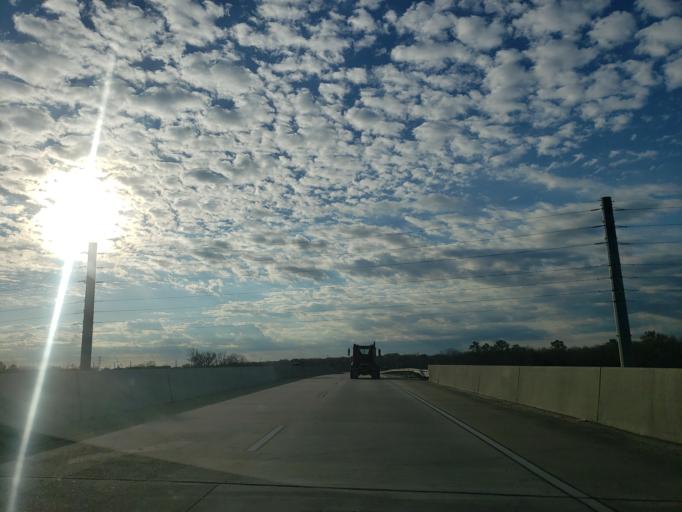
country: US
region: Georgia
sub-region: Chatham County
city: Port Wentworth
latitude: 32.1370
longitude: -81.1662
